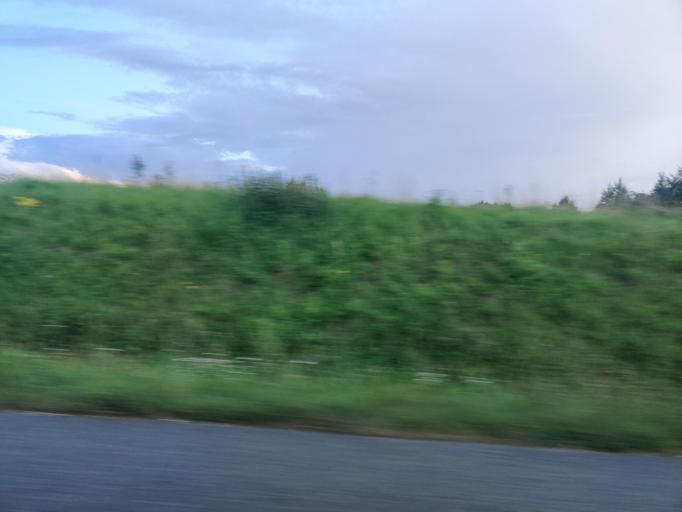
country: PL
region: Greater Poland Voivodeship
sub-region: Konin
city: Konin
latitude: 52.1954
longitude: 18.3097
